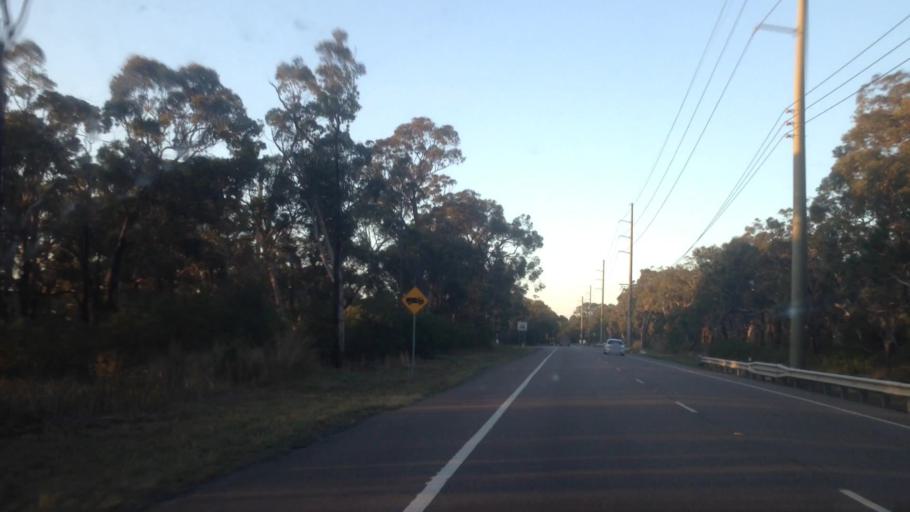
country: AU
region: New South Wales
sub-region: Wyong Shire
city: Kingfisher Shores
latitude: -33.1814
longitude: 151.5386
